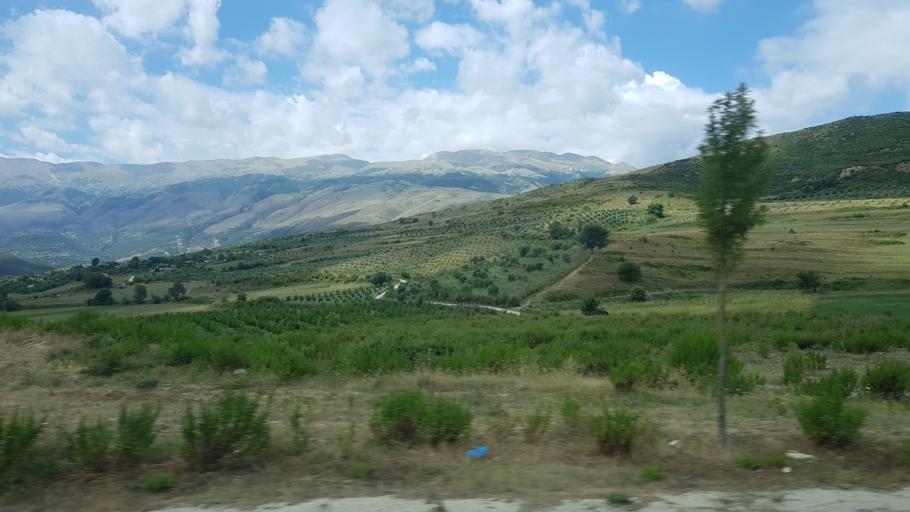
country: AL
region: Gjirokaster
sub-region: Rrethi i Tepelenes
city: Krahes
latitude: 40.4049
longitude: 19.8614
